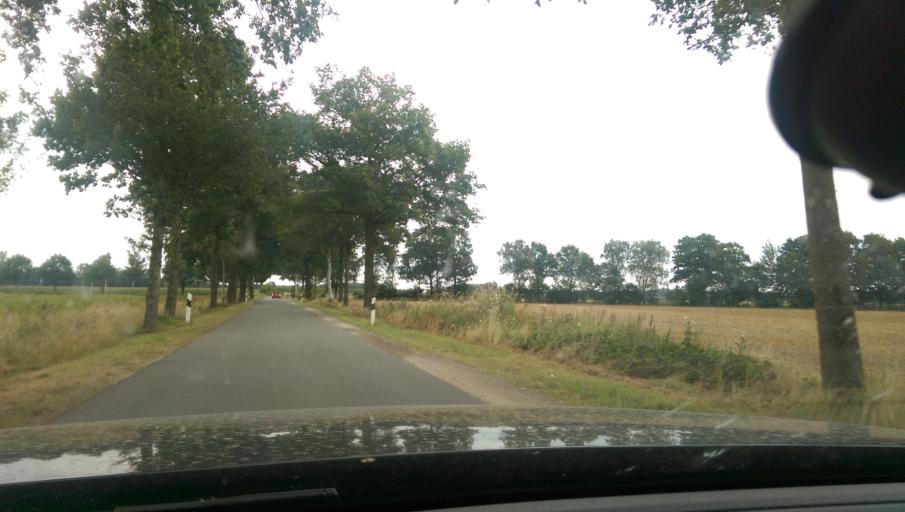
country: DE
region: Lower Saxony
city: Lindwedel
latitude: 52.5879
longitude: 9.6301
